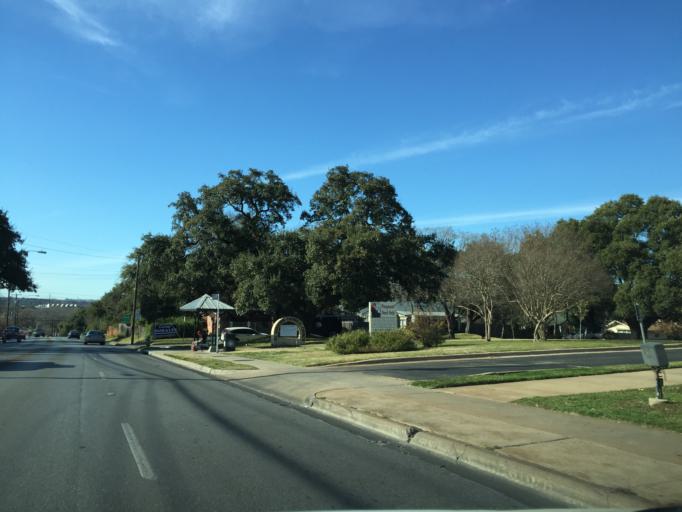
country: US
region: Texas
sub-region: Travis County
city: Austin
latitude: 30.2399
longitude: -97.7552
